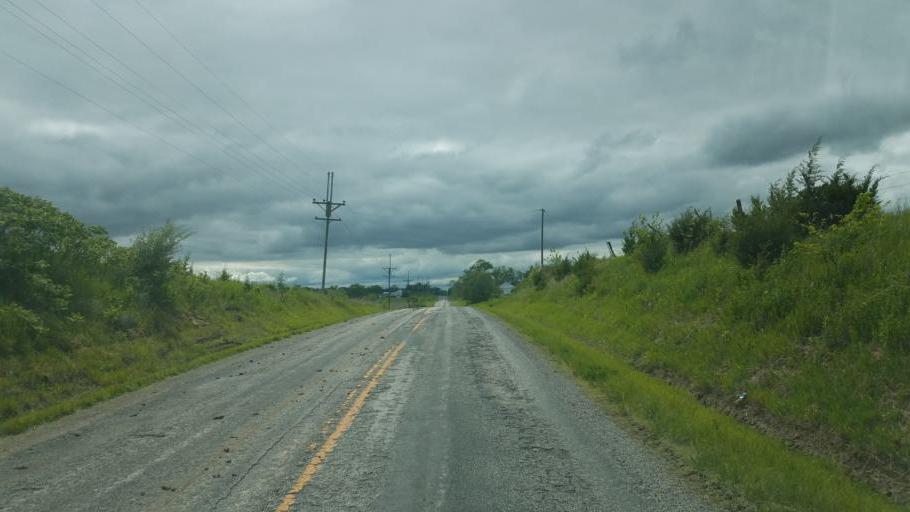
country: US
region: Iowa
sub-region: Decatur County
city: Lamoni
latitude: 40.4237
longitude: -93.8202
